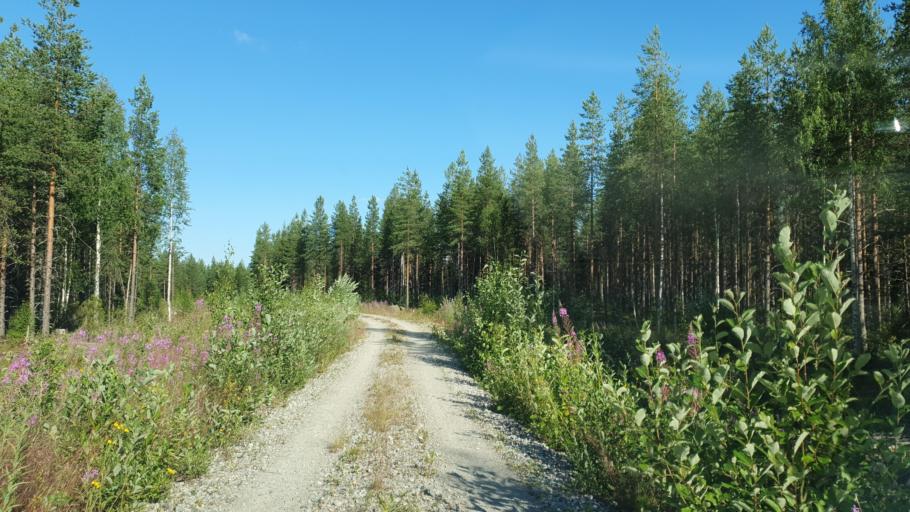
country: FI
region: Kainuu
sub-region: Kehys-Kainuu
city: Kuhmo
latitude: 64.0032
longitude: 29.7596
